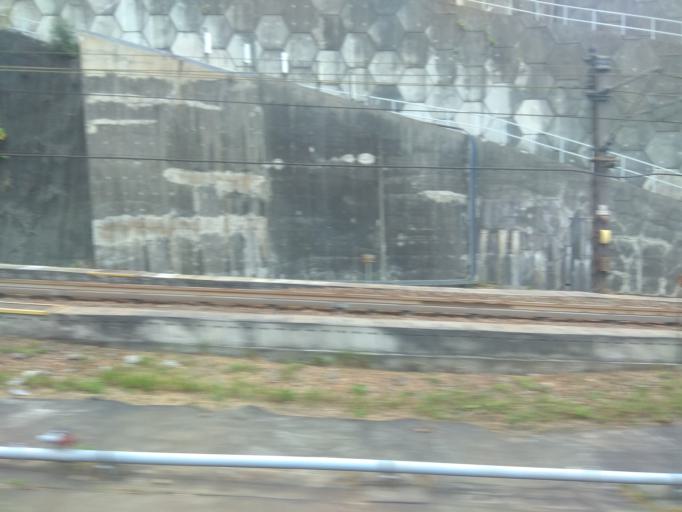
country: HK
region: Tsuen Wan
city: Tsuen Wan
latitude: 22.3397
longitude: 114.0417
